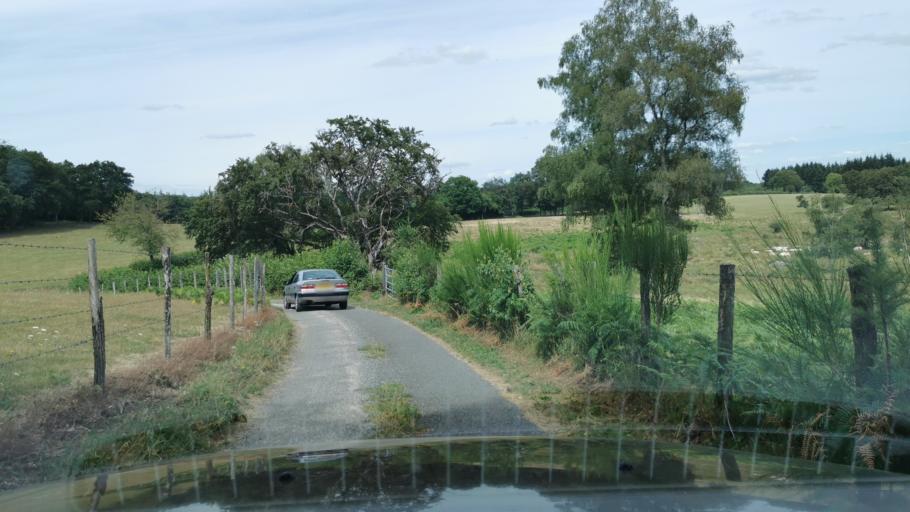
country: FR
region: Bourgogne
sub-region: Departement de Saone-et-Loire
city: Marmagne
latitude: 46.8065
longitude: 4.2775
